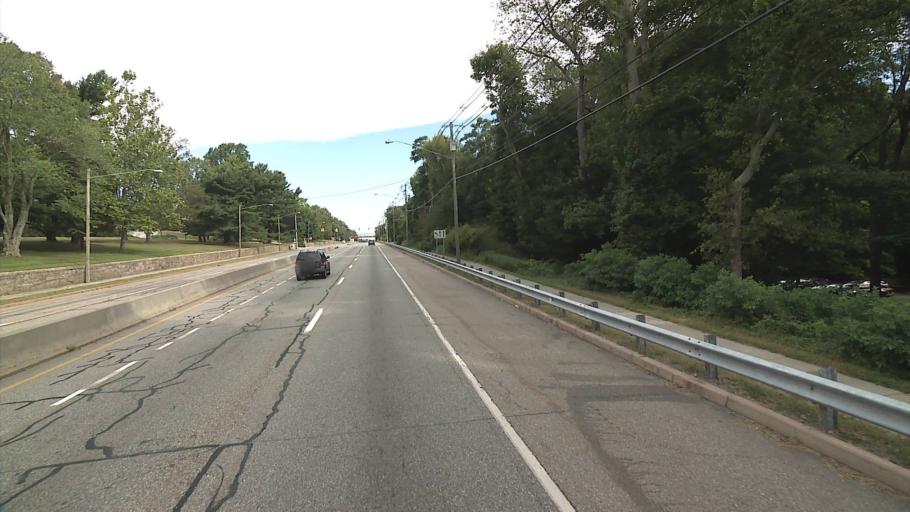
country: US
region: Connecticut
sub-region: New London County
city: New London
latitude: 41.3771
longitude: -72.1031
